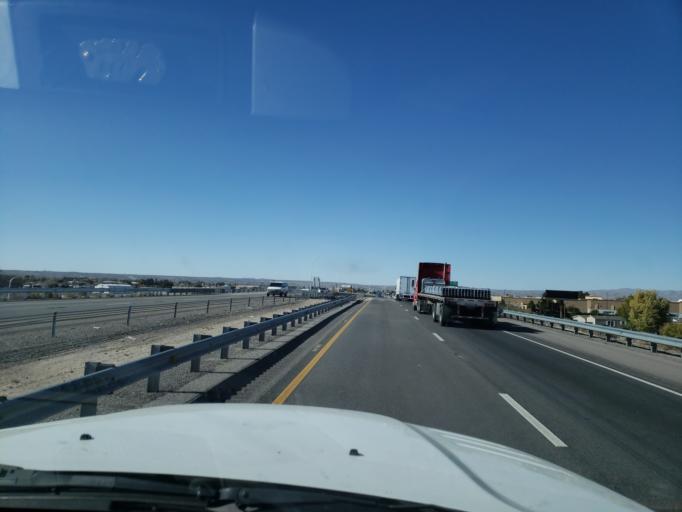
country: US
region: New Mexico
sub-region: Dona Ana County
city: Mesilla
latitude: 32.2857
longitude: -106.7820
